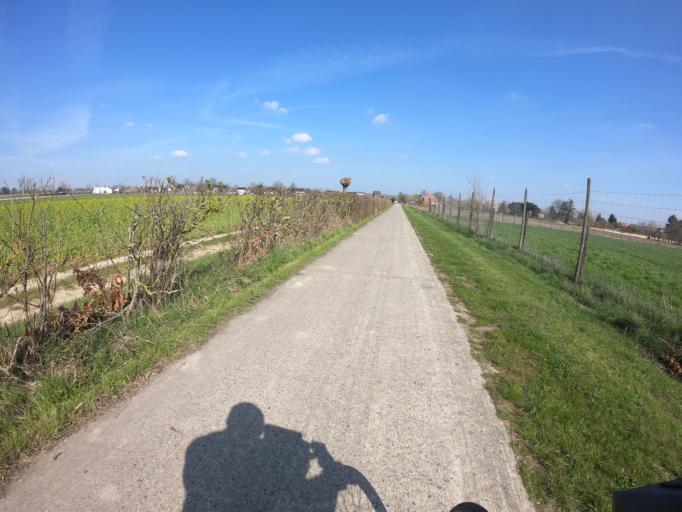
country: BE
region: Flanders
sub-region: Provincie Vlaams-Brabant
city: Geetbets
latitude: 50.9040
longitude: 5.1120
